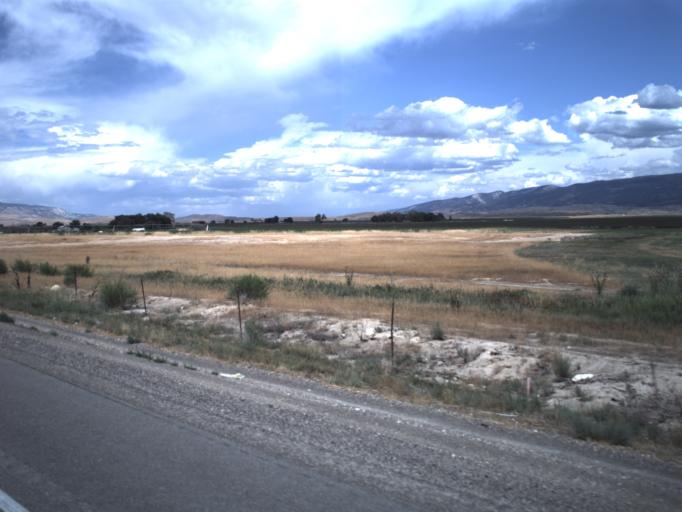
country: US
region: Utah
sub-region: Sanpete County
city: Centerfield
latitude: 39.0636
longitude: -111.8208
